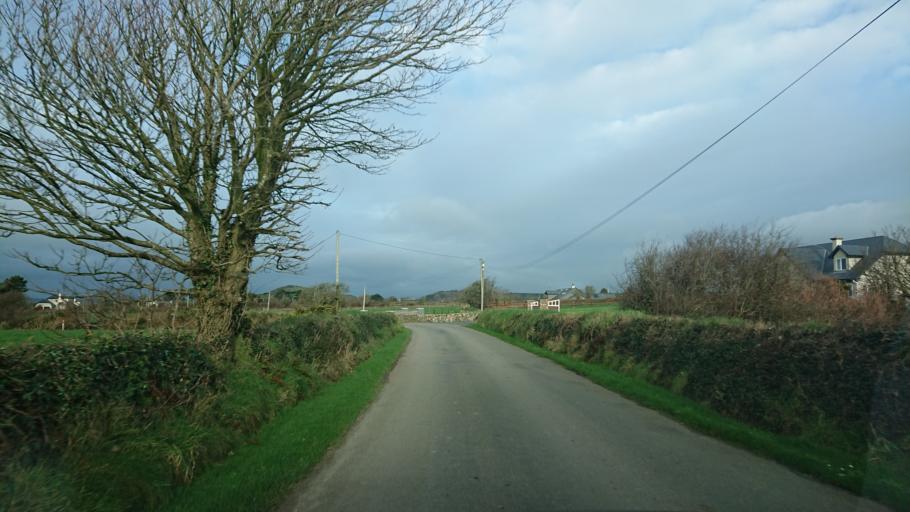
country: IE
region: Munster
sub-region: Waterford
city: Tra Mhor
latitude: 52.1510
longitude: -7.2123
